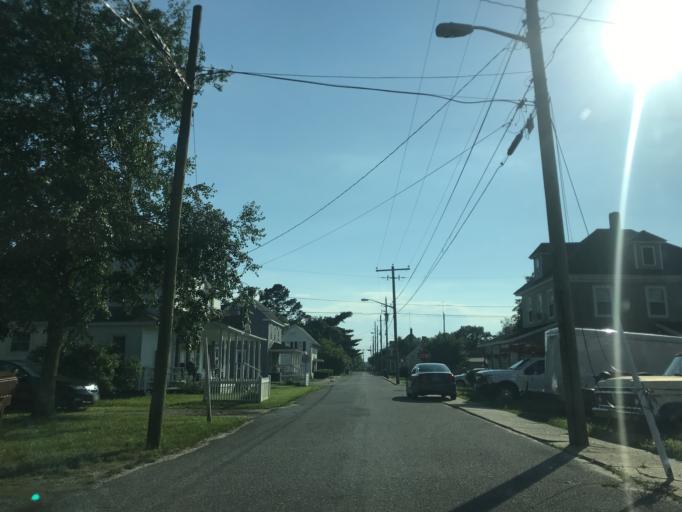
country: US
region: Maryland
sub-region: Wicomico County
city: Hebron
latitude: 38.5430
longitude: -75.7175
